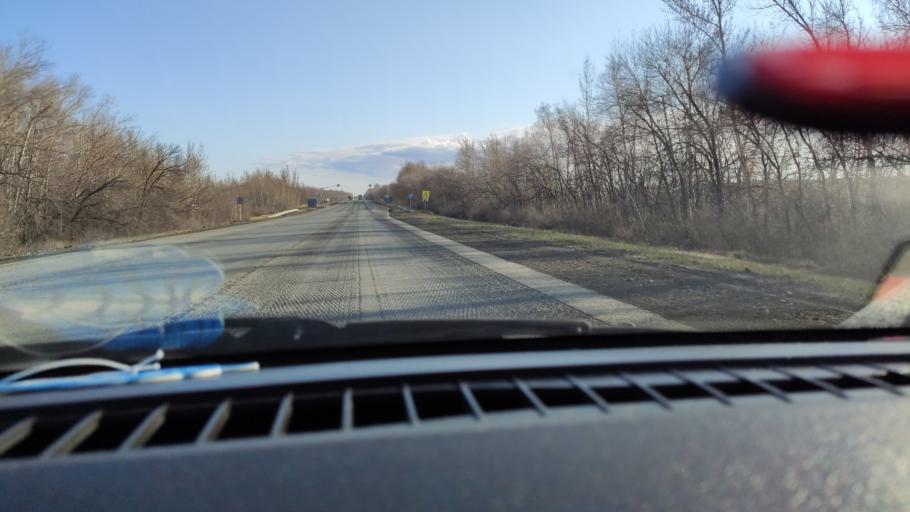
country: RU
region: Saratov
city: Dukhovnitskoye
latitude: 52.6604
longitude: 48.2104
